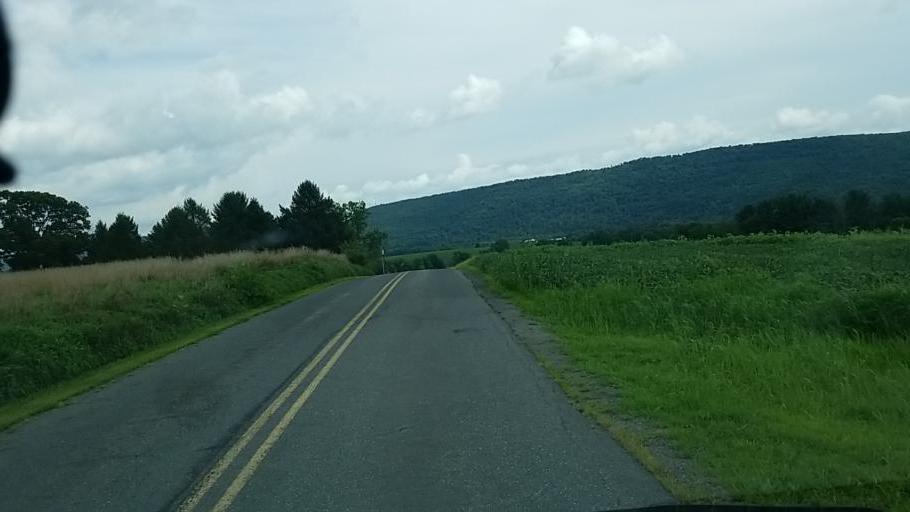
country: US
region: Pennsylvania
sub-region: Dauphin County
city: Elizabethville
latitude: 40.6479
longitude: -76.8318
